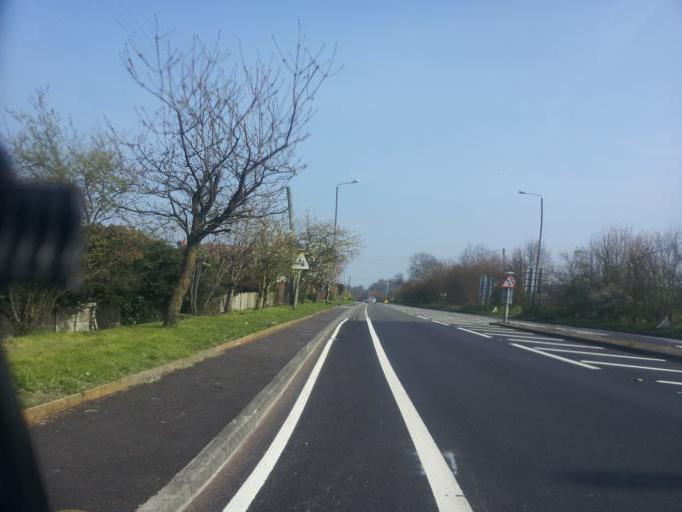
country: GB
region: England
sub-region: Medway
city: Cuxton
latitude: 51.4195
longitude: 0.4356
